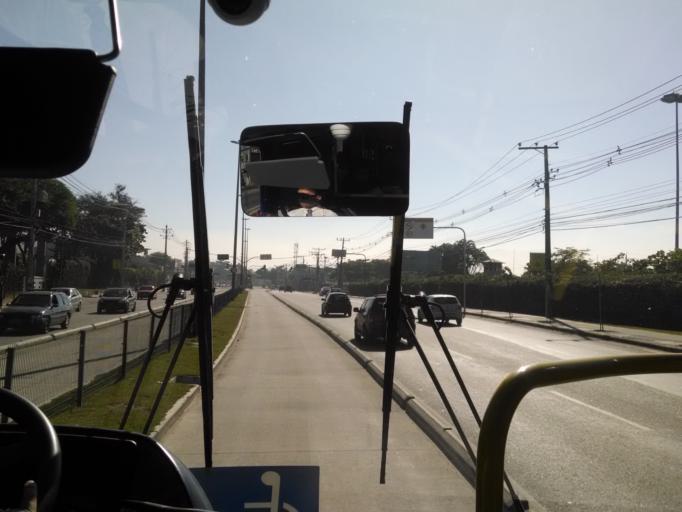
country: BR
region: Rio de Janeiro
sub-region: Sao Joao De Meriti
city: Sao Joao de Meriti
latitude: -22.9505
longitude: -43.3732
